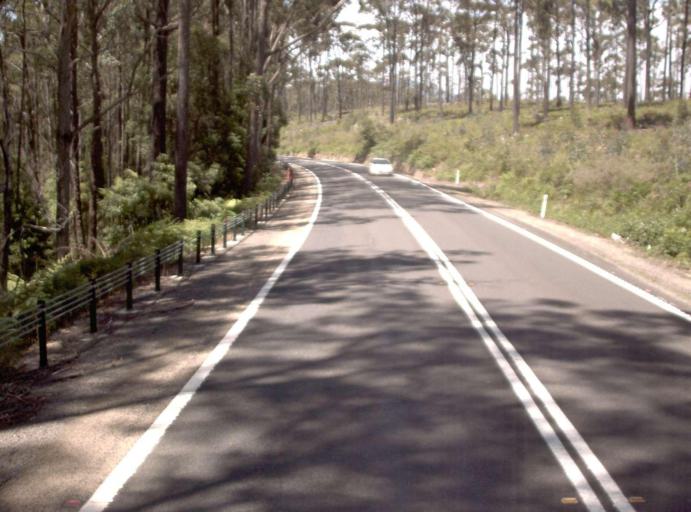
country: AU
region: Victoria
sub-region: East Gippsland
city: Lakes Entrance
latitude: -37.6587
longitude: 148.8055
